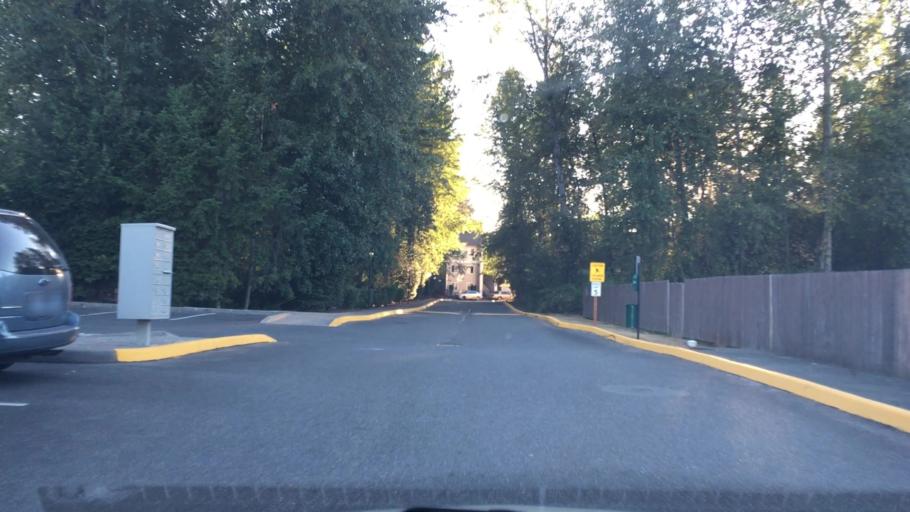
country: US
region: Washington
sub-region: King County
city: Lea Hill
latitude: 47.3257
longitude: -122.1770
